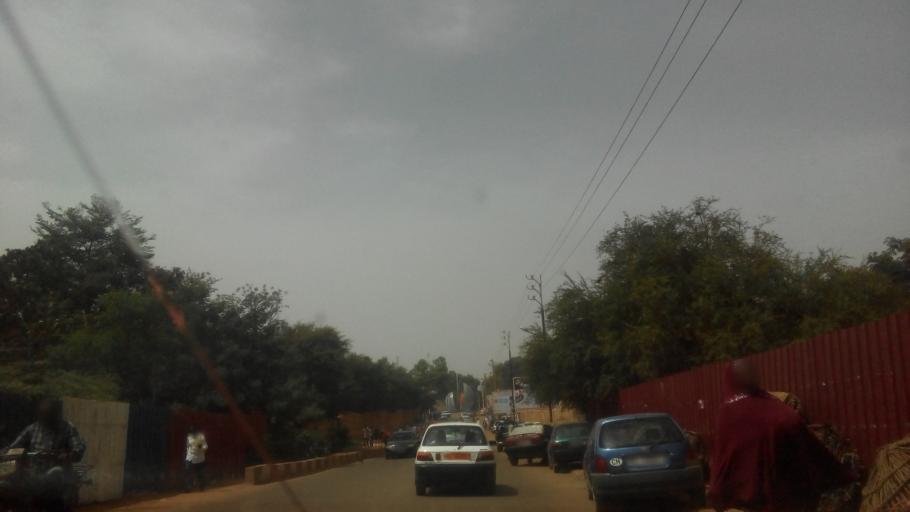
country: NE
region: Niamey
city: Niamey
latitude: 13.5151
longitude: 2.1071
